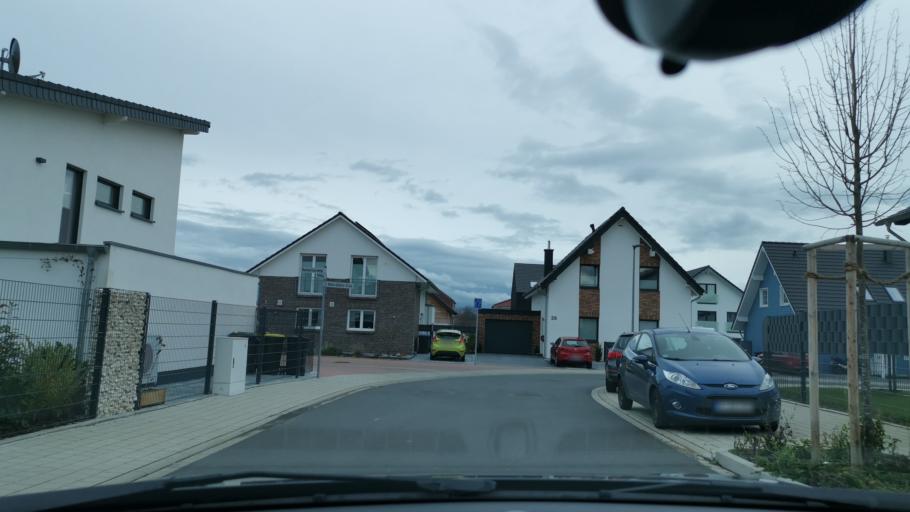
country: DE
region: North Rhine-Westphalia
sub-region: Regierungsbezirk Dusseldorf
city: Rommerskirchen
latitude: 51.0394
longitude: 6.6900
